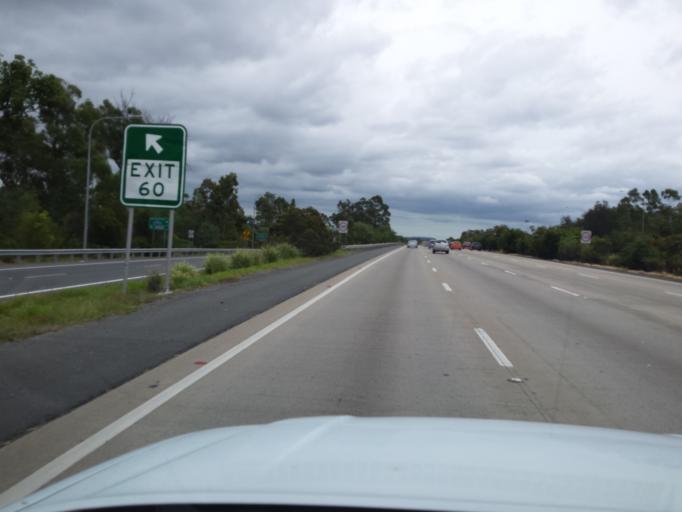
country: AU
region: Queensland
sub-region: Gold Coast
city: Upper Coomera
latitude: -27.9121
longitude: 153.3186
